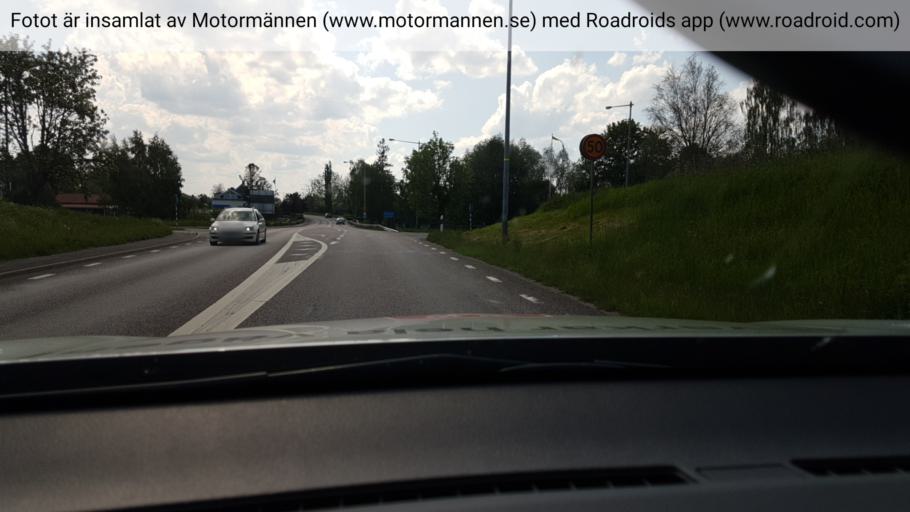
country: SE
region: Vaestra Goetaland
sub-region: Falkopings Kommun
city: Falkoeping
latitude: 58.0282
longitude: 13.5496
